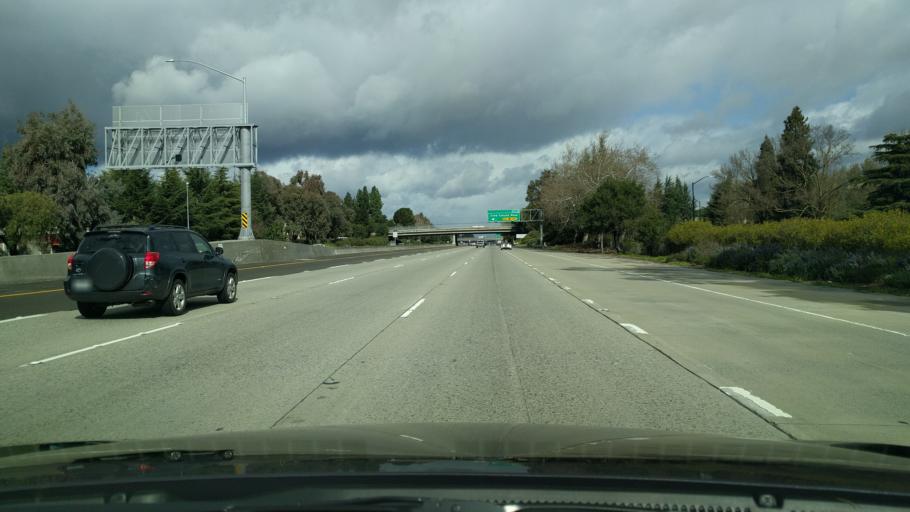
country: US
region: California
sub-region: Contra Costa County
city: San Ramon
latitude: 37.7689
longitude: -121.9709
